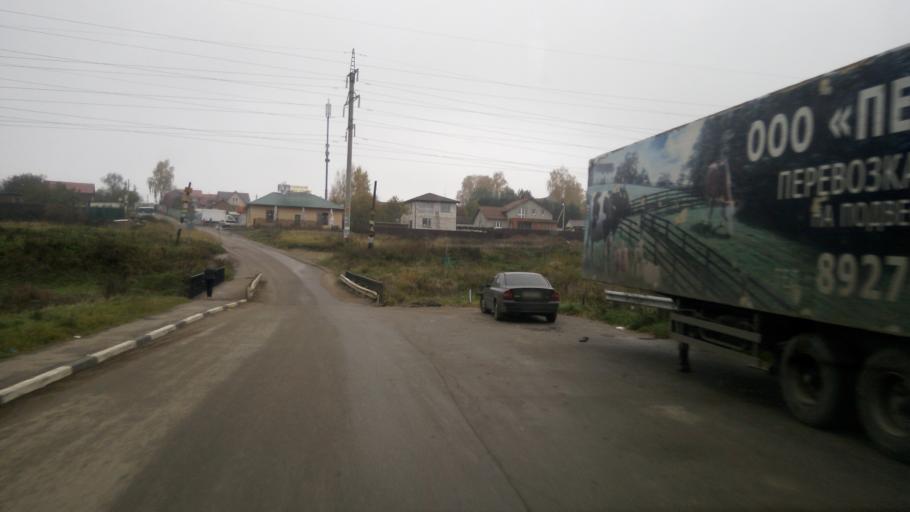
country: RU
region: Moskovskaya
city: Skhodnya
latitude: 55.9359
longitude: 37.2882
